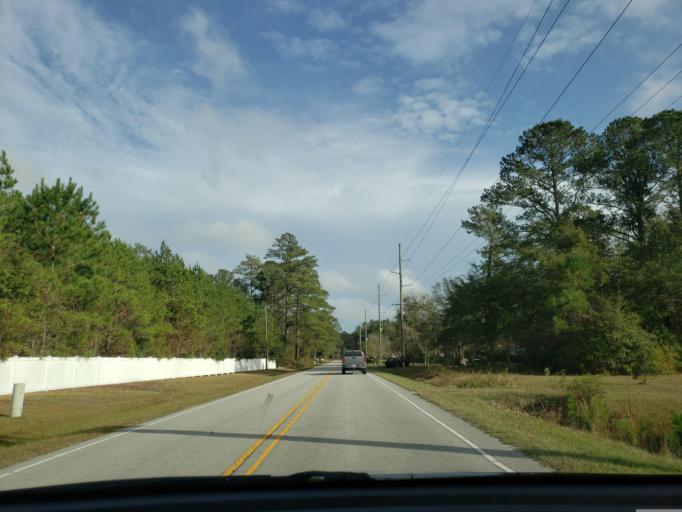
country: US
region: North Carolina
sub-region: Onslow County
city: Jacksonville
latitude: 34.6868
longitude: -77.5300
